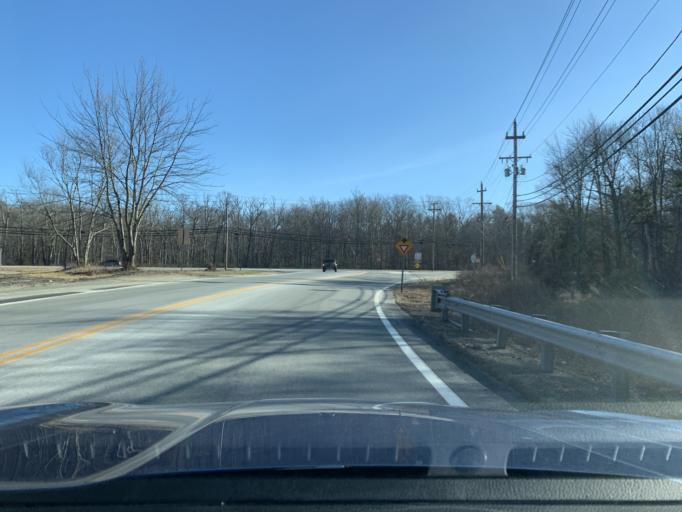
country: US
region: Rhode Island
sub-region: Kent County
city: West Greenwich
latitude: 41.5964
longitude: -71.6483
